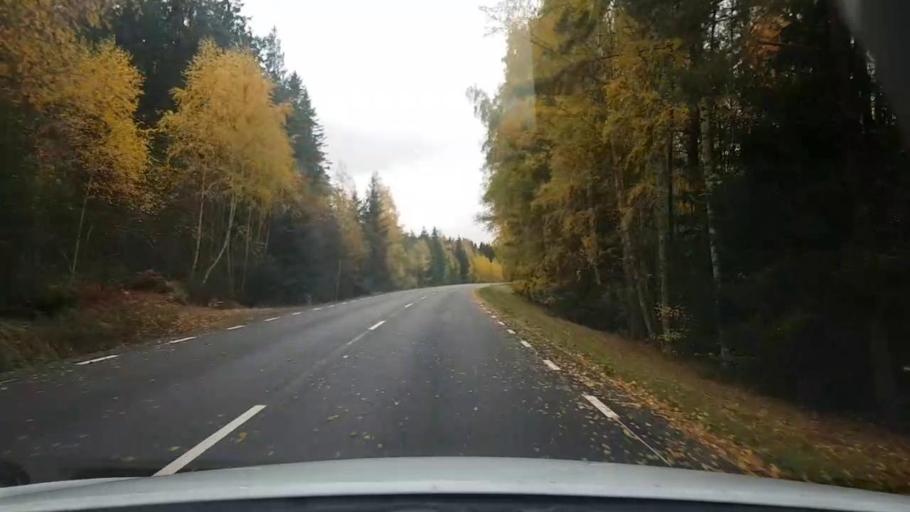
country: SE
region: OErebro
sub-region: Laxa Kommun
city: Laxa
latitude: 58.7736
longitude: 14.5360
